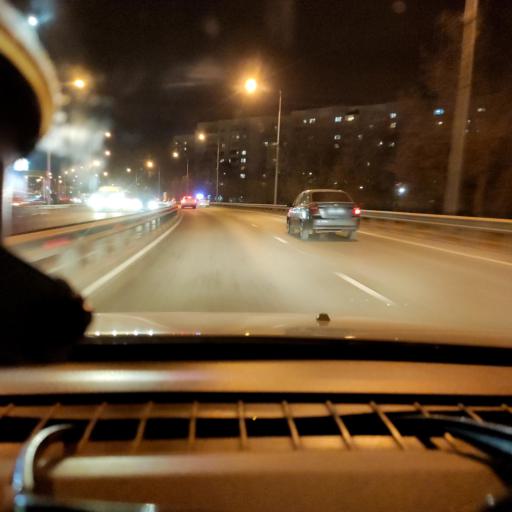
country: RU
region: Samara
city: Volzhskiy
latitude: 53.3528
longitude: 50.2125
